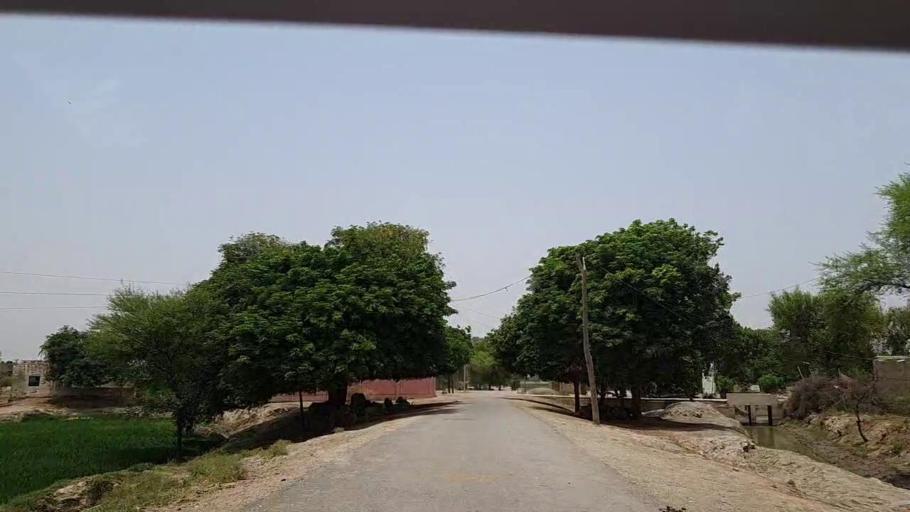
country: PK
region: Sindh
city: Khairpur Nathan Shah
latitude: 27.0171
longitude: 67.6694
